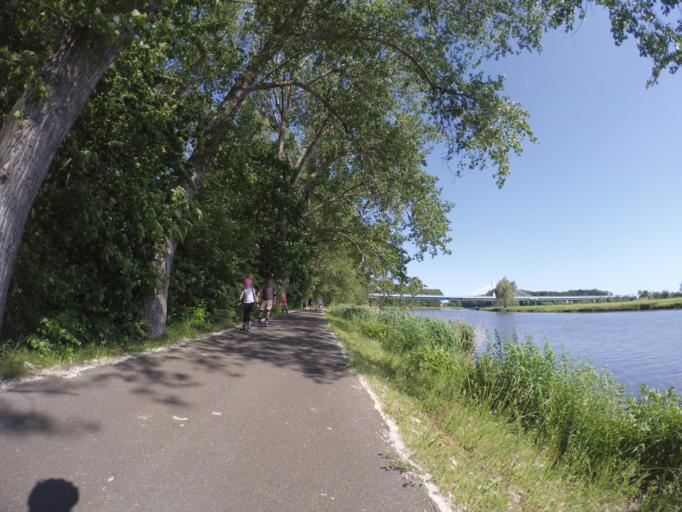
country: CZ
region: Central Bohemia
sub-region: Okres Nymburk
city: Podebrady
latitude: 50.1675
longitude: 15.0866
